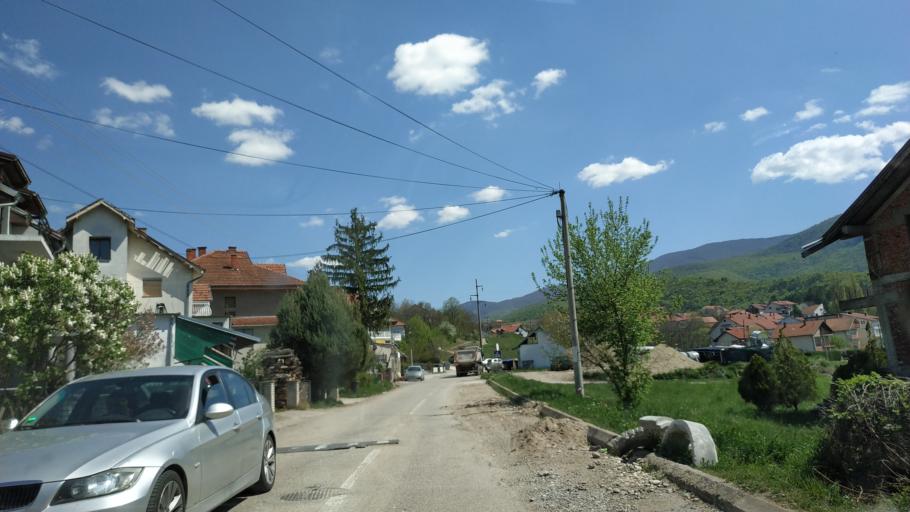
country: RS
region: Central Serbia
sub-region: Zajecarski Okrug
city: Soko Banja
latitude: 43.6482
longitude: 21.8810
